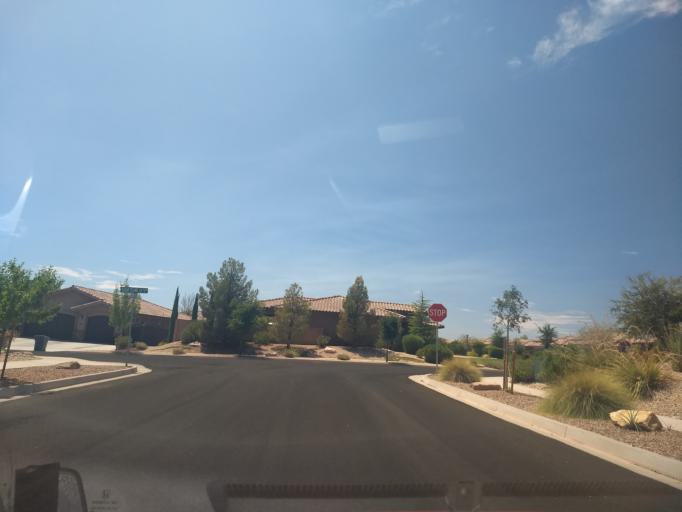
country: US
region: Utah
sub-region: Washington County
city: Washington
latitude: 37.1400
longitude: -113.4828
